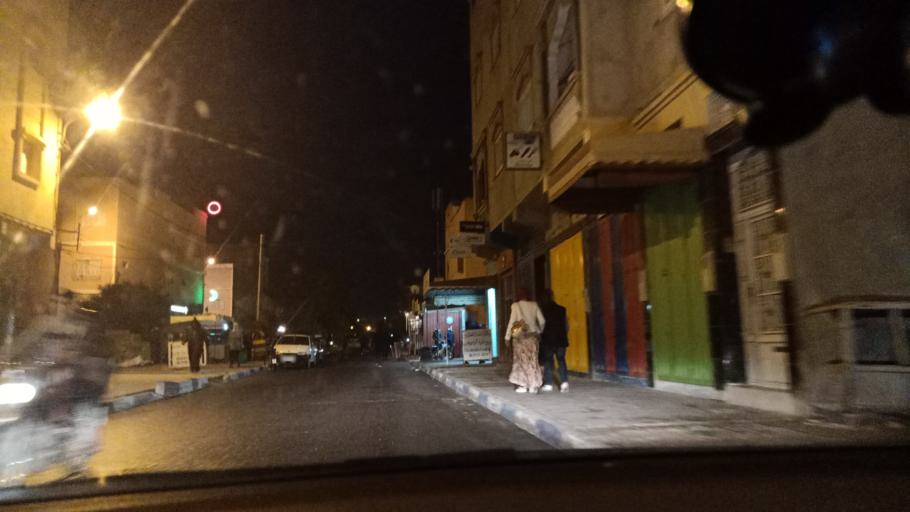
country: MA
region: Doukkala-Abda
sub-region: Safi
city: Youssoufia
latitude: 32.2519
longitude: -8.5344
